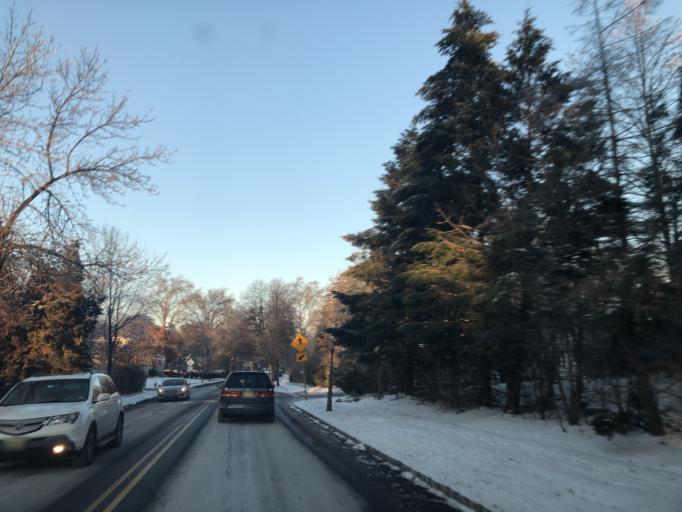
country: US
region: New Jersey
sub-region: Essex County
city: Irvington
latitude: 40.7491
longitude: -74.2406
